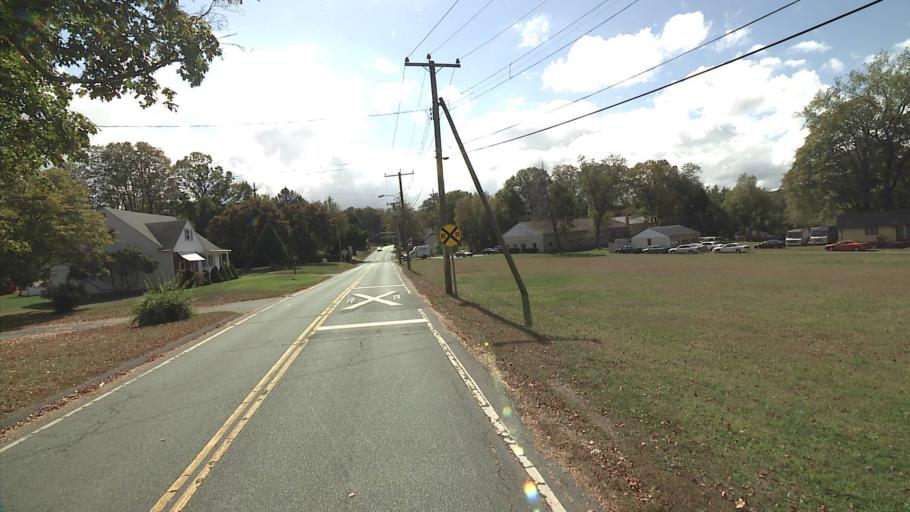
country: US
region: Connecticut
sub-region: Middlesex County
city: Middletown
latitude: 41.5448
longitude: -72.6827
